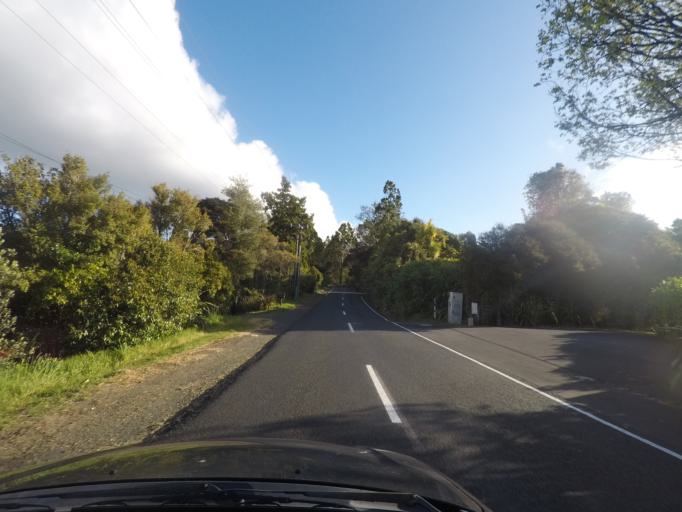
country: NZ
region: Auckland
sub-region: Auckland
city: Titirangi
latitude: -36.9295
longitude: 174.6190
